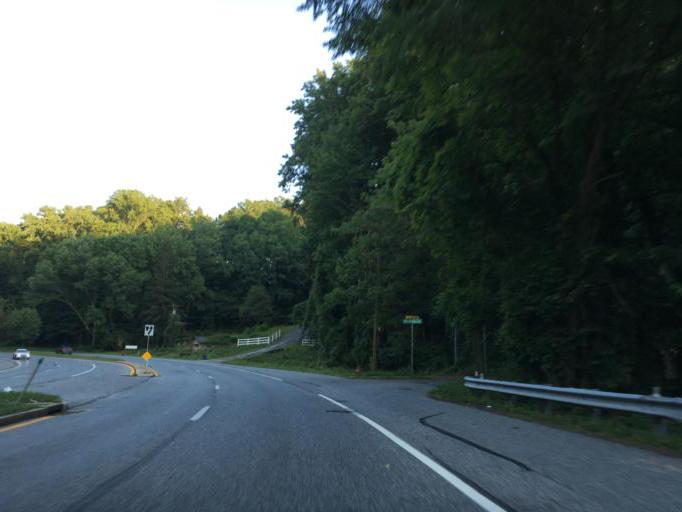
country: US
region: Maryland
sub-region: Baltimore County
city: Towson
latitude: 39.3902
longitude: -76.6285
